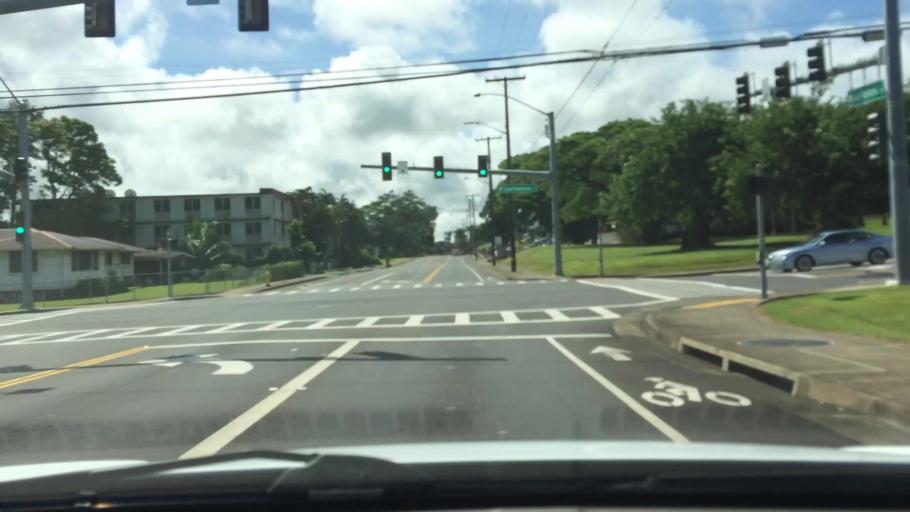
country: US
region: Hawaii
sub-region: Hawaii County
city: Hilo
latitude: 19.7048
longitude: -155.0797
